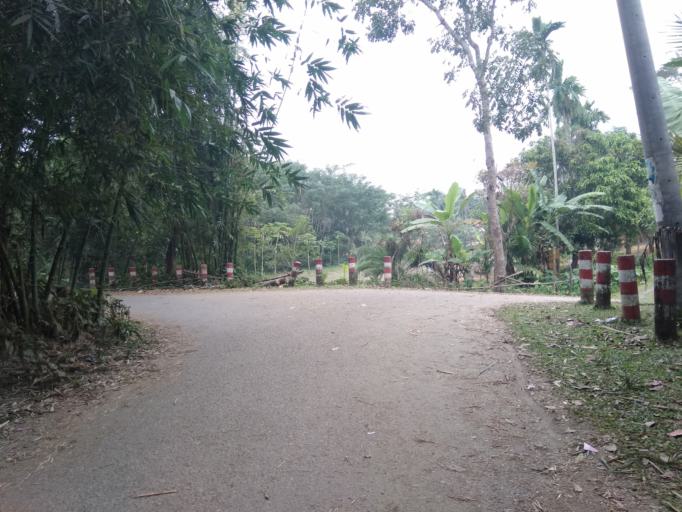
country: BD
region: Barisal
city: Mehendiganj
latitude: 22.9225
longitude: 90.3919
